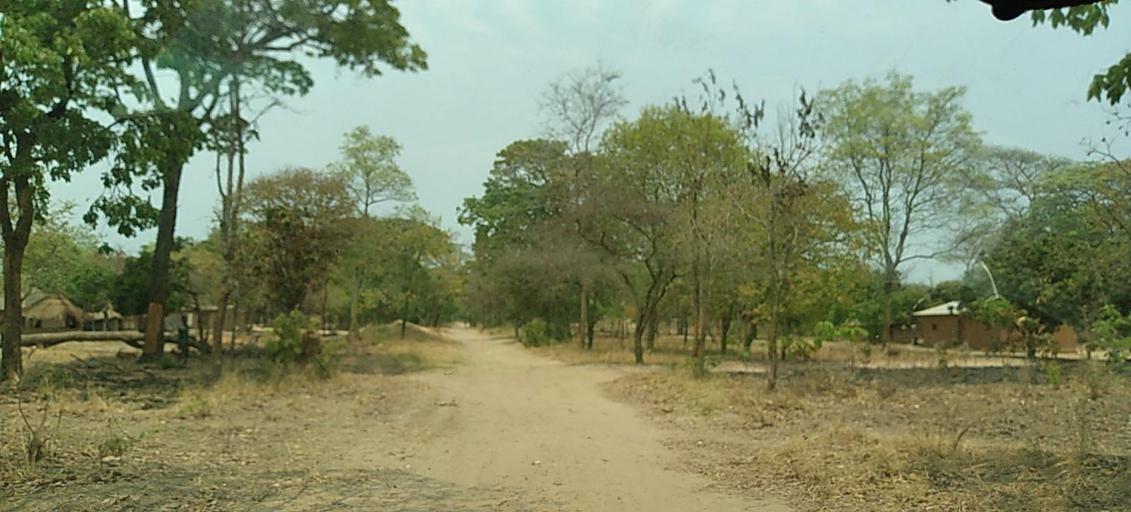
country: ZM
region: North-Western
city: Kabompo
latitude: -13.5575
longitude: 24.4470
